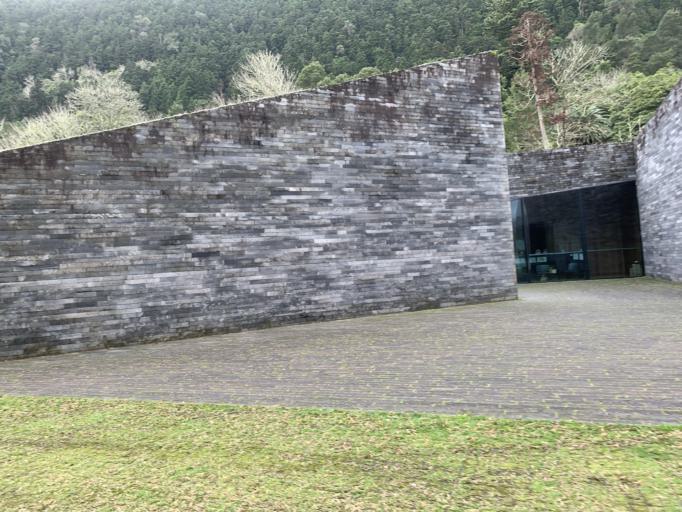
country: PT
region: Azores
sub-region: Povoacao
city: Furnas
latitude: 37.7515
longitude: -25.3375
